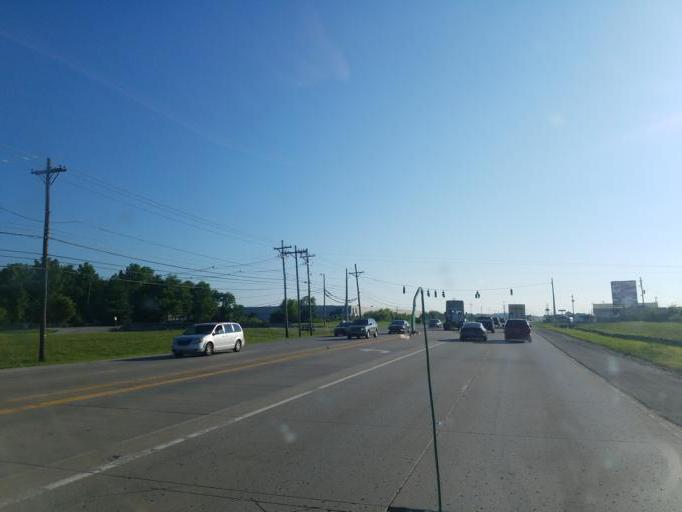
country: US
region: Kentucky
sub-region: Jefferson County
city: Heritage Creek
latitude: 38.1330
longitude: -85.7255
